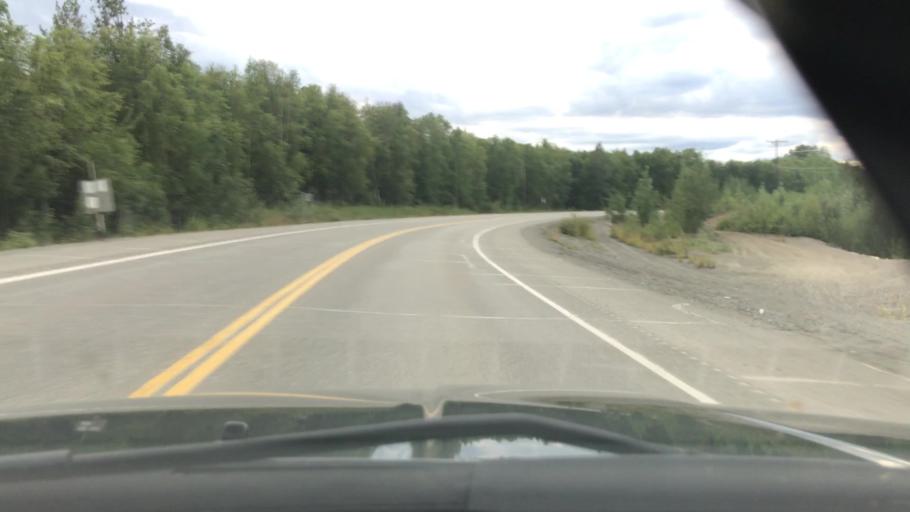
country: US
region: Alaska
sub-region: Matanuska-Susitna Borough
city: Y
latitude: 62.1387
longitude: -150.0536
